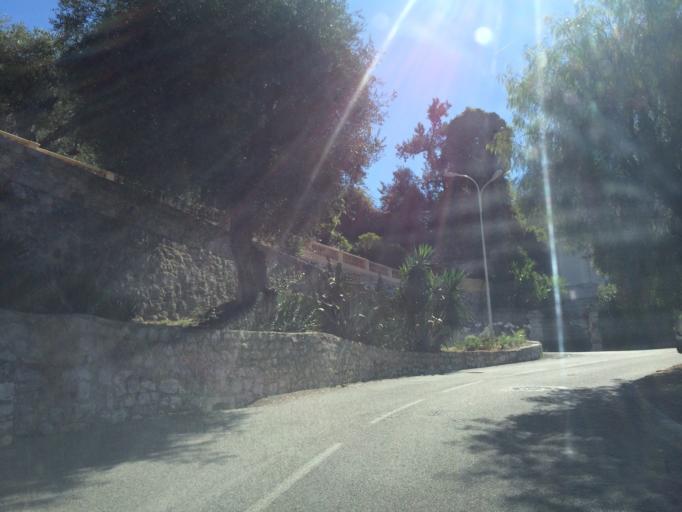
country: FR
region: Provence-Alpes-Cote d'Azur
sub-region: Departement des Alpes-Maritimes
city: Villefranche-sur-Mer
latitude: 43.7088
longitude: 7.3141
